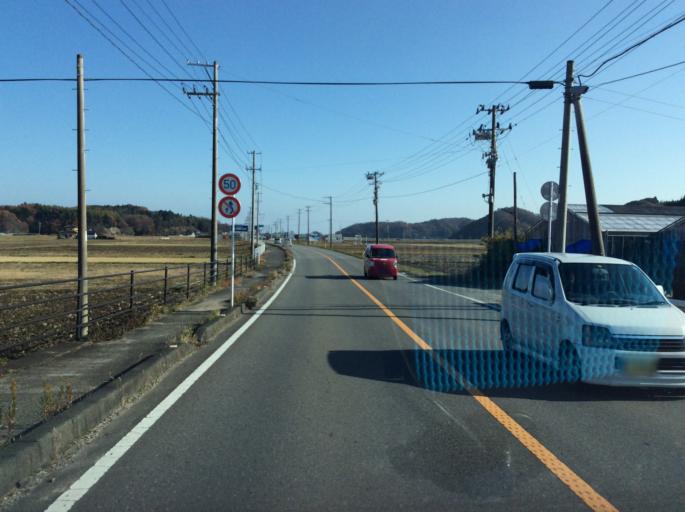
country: JP
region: Fukushima
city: Iwaki
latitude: 37.0325
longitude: 140.9309
